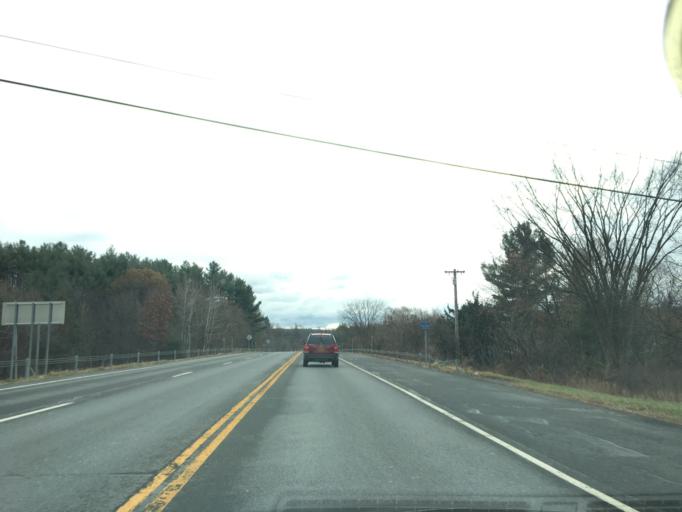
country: US
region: New York
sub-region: Rensselaer County
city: Poestenkill
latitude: 42.6636
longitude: -73.5792
